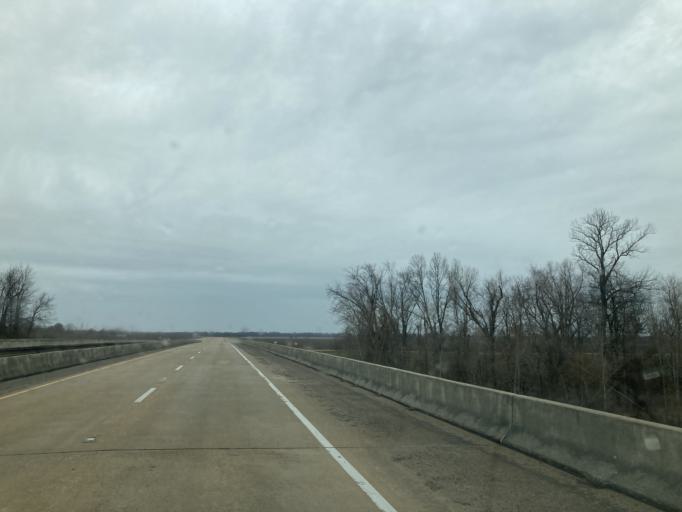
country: US
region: Mississippi
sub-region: Humphreys County
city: Belzoni
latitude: 33.0536
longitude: -90.4685
